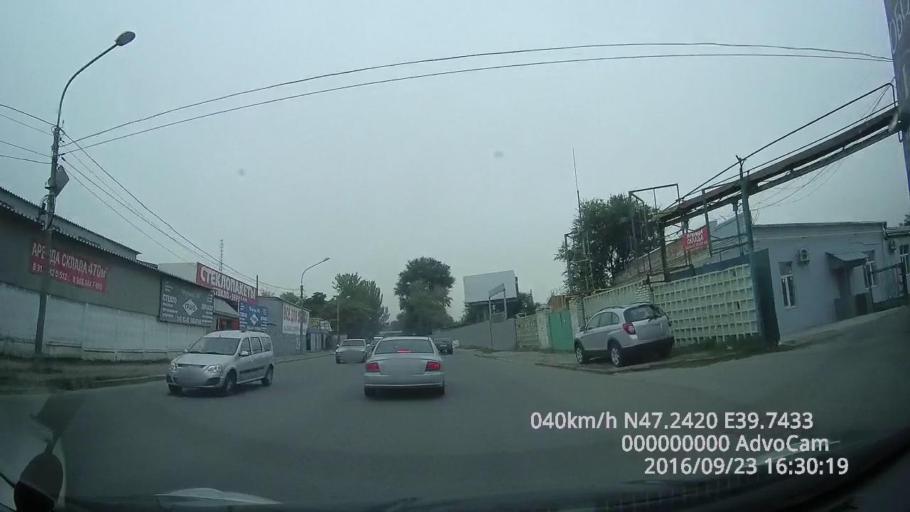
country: RU
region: Rostov
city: Rostov-na-Donu
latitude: 47.2420
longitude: 39.7431
